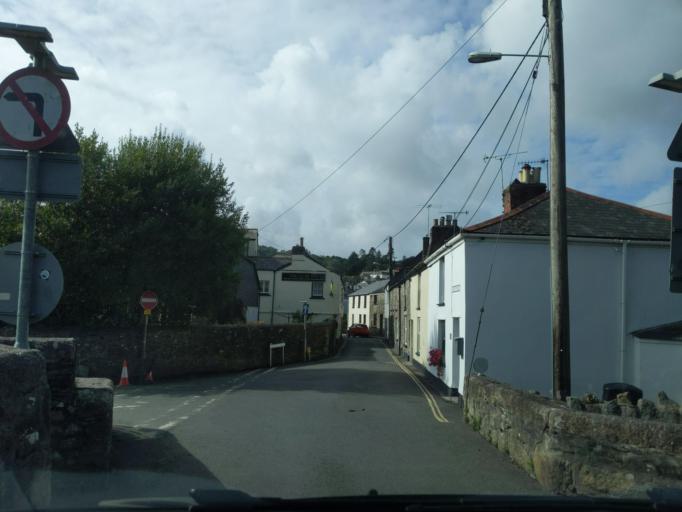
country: GB
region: England
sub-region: Cornwall
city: Lostwithiel
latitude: 50.4076
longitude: -4.6670
